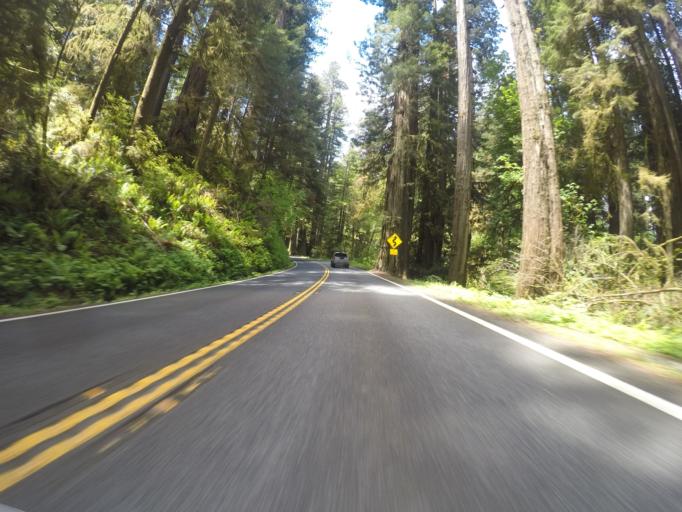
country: US
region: California
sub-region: Del Norte County
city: Bertsch-Oceanview
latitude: 41.8113
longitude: -124.1098
